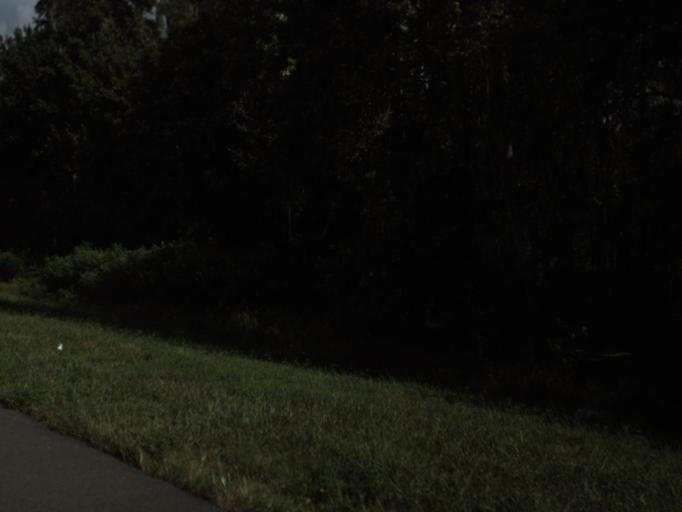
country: US
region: Florida
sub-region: Polk County
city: Kathleen
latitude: 28.1808
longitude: -81.9930
